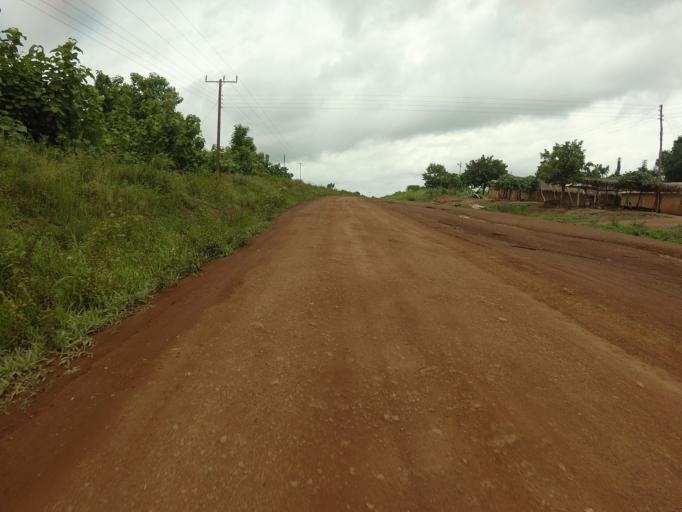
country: GH
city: Kpandae
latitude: 8.3121
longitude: 0.4823
